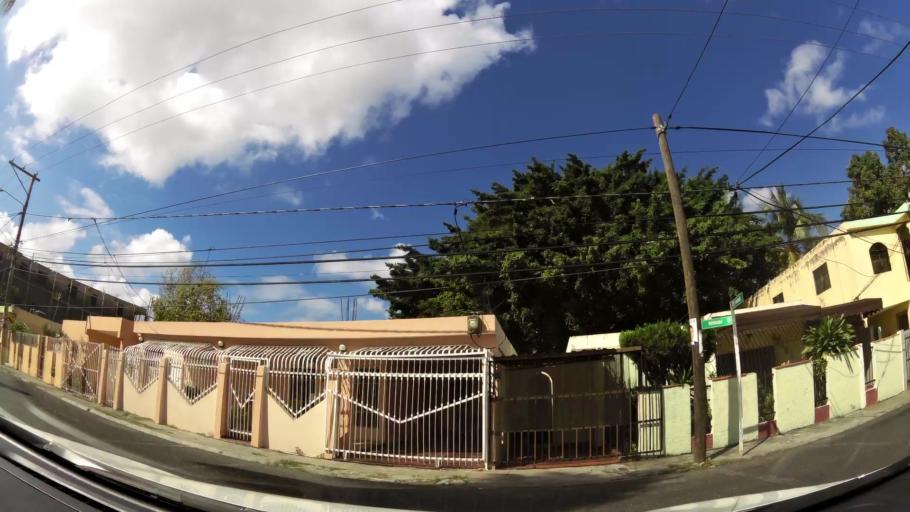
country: DO
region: Santo Domingo
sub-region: Santo Domingo
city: Santo Domingo Este
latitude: 18.5085
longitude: -69.8503
